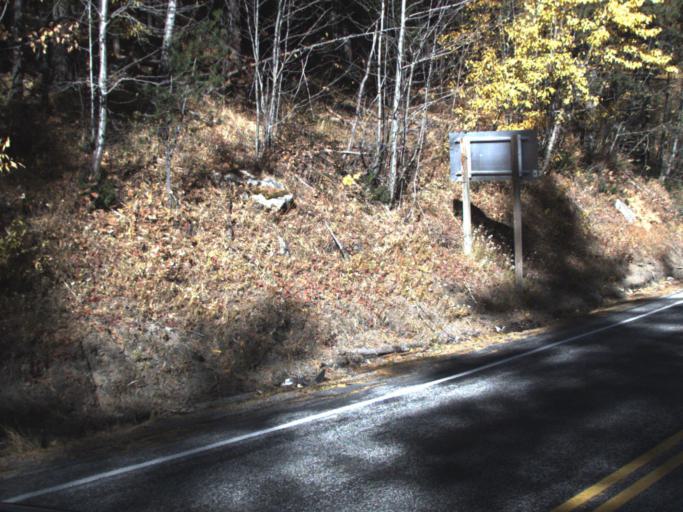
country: US
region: Washington
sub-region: Ferry County
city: Republic
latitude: 48.6258
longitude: -118.4435
